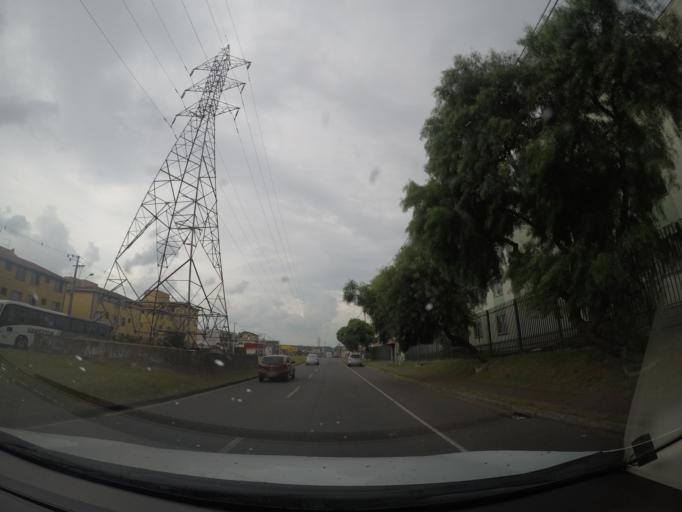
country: BR
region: Parana
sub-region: Sao Jose Dos Pinhais
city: Sao Jose dos Pinhais
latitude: -25.5486
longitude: -49.2589
